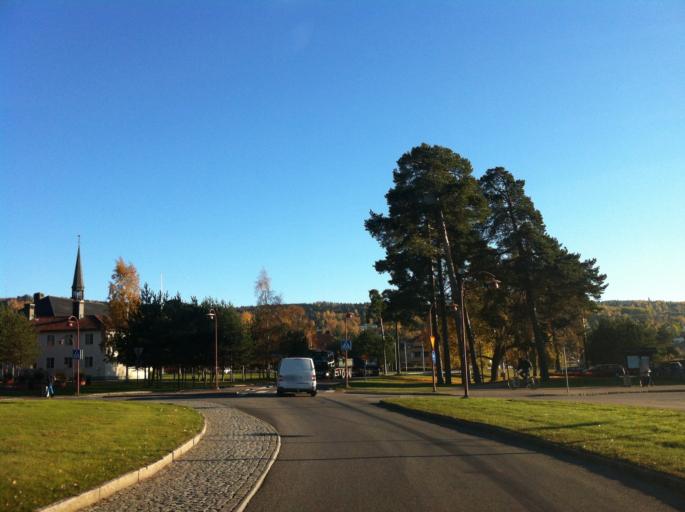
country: SE
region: Dalarna
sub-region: Rattviks Kommun
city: Raettvik
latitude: 60.8859
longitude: 15.1159
